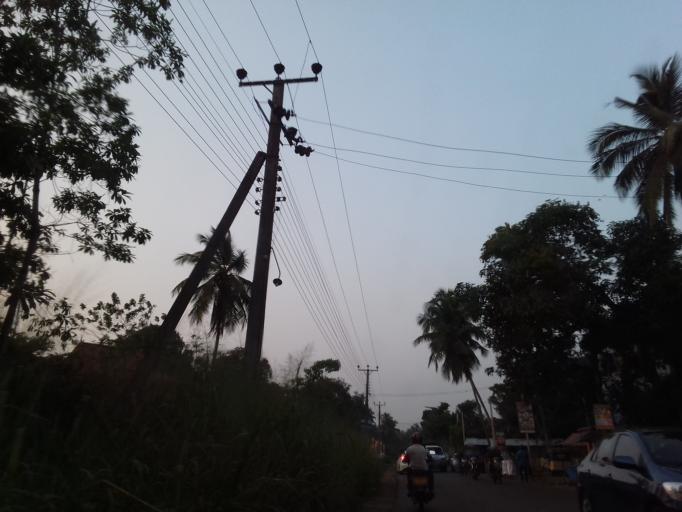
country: LK
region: Western
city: Welisara
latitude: 7.0431
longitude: 79.9574
